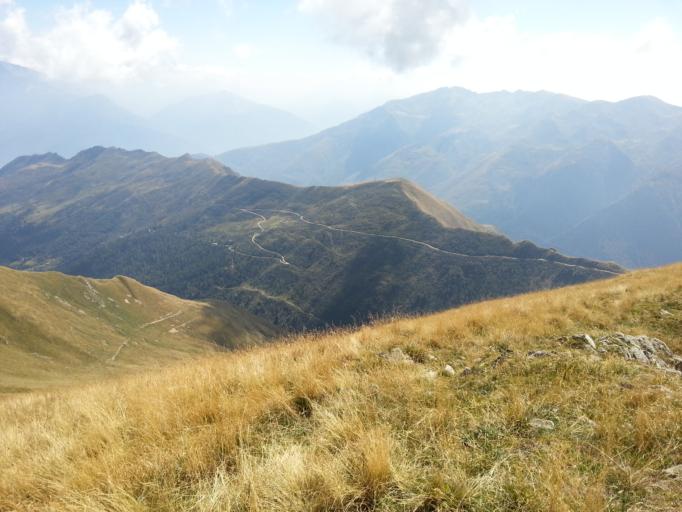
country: CH
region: Grisons
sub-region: Moesa District
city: Roveredo
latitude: 46.1689
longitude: 9.1720
